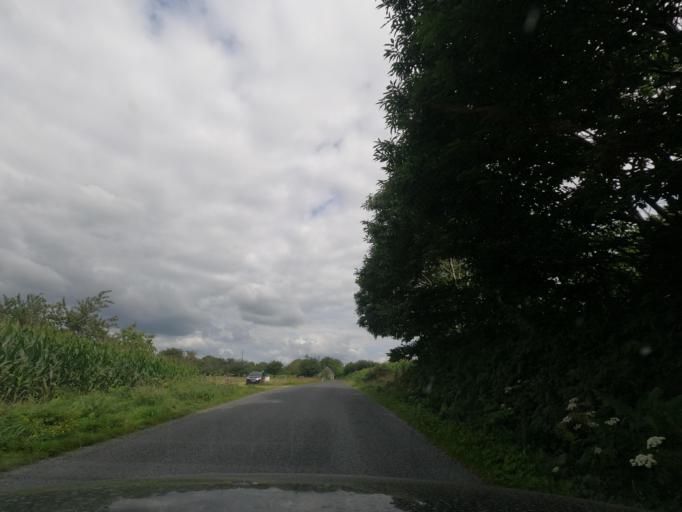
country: FR
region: Pays de la Loire
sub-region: Departement de la Mayenne
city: Fougerolles-du-Plessis
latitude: 48.4926
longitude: -0.9435
